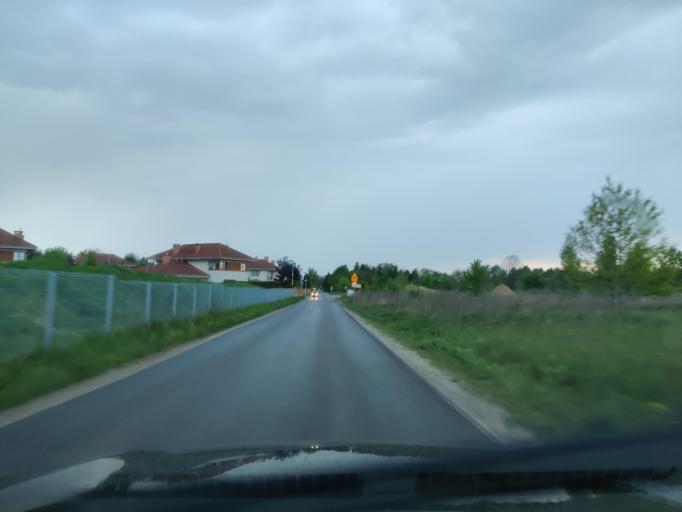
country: PL
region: Masovian Voivodeship
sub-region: Powiat piaseczynski
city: Konstancin-Jeziorna
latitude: 52.1117
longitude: 21.1239
